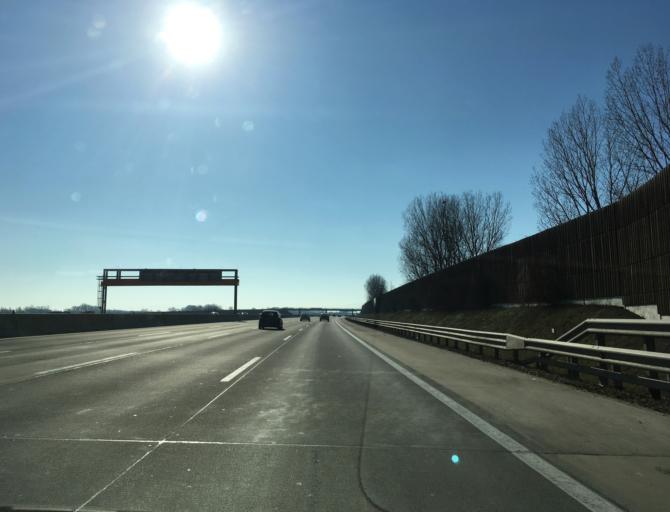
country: AT
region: Lower Austria
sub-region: Politischer Bezirk Baden
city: Trumau
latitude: 48.0176
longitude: 16.3255
